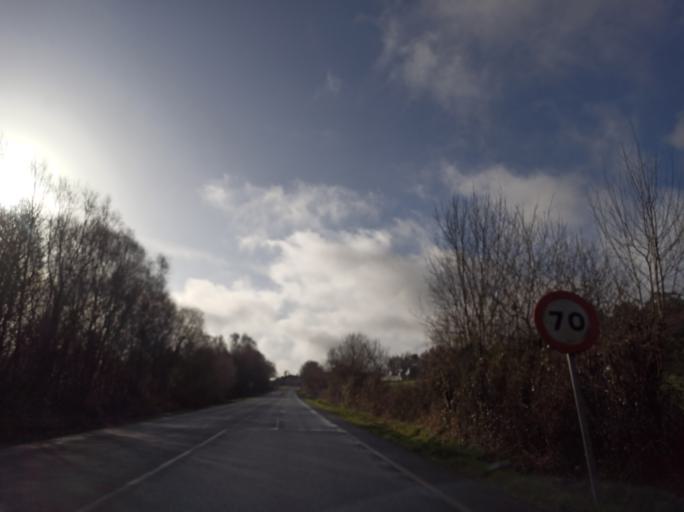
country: ES
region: Galicia
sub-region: Provincia da Coruna
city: Sobrado
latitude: 43.0825
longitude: -8.0141
